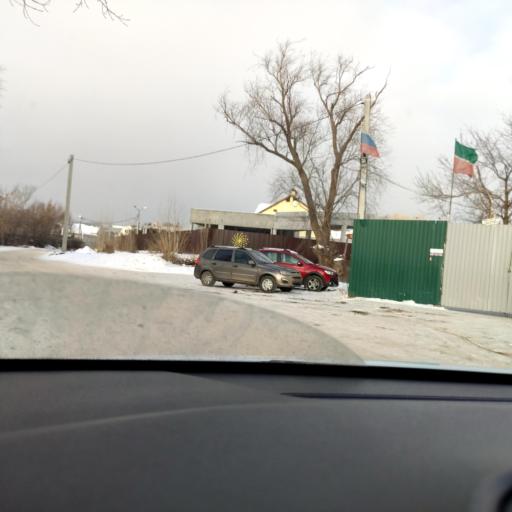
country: RU
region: Tatarstan
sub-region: Gorod Kazan'
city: Kazan
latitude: 55.7914
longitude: 49.0604
